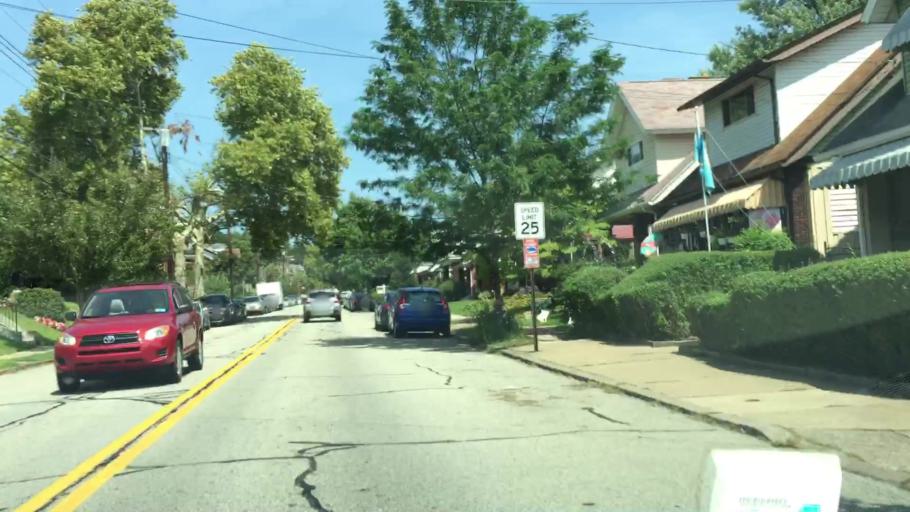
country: US
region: Pennsylvania
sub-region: Allegheny County
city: Sharpsburg
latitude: 40.4828
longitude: -79.9296
